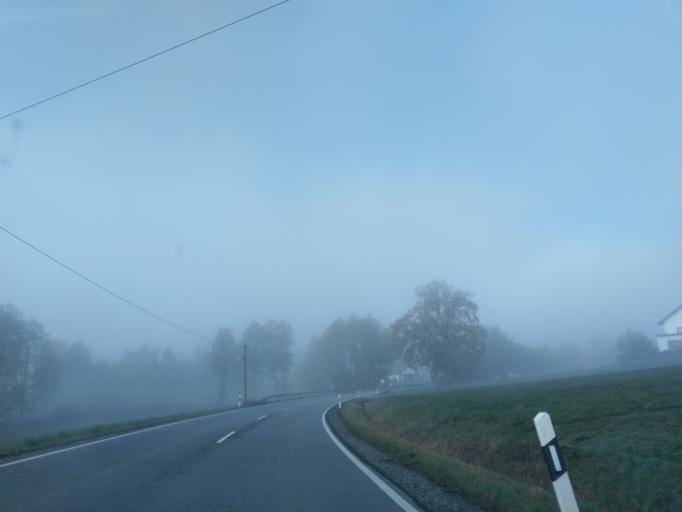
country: DE
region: Bavaria
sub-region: Lower Bavaria
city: Schollnach
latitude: 48.7303
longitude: 13.1748
